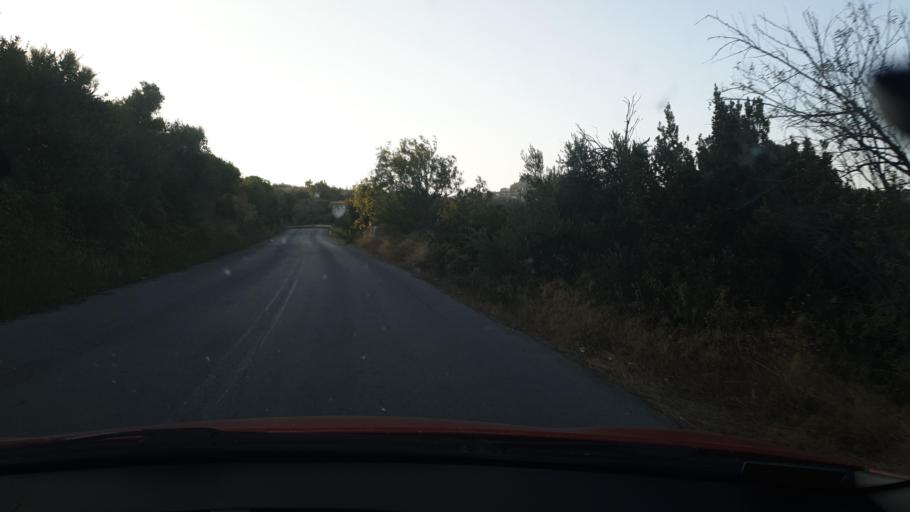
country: GR
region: Central Greece
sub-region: Nomos Evvoias
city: Oxilithos
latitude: 38.5723
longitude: 24.1204
